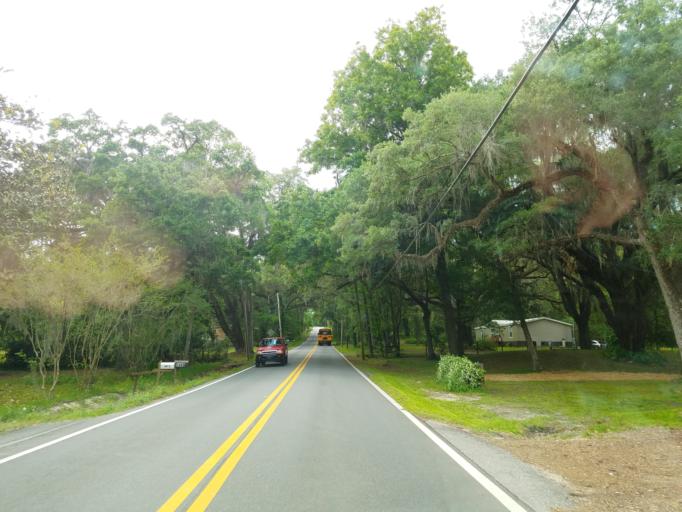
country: US
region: Florida
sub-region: Hernando County
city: Brooksville
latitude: 28.5562
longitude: -82.3678
